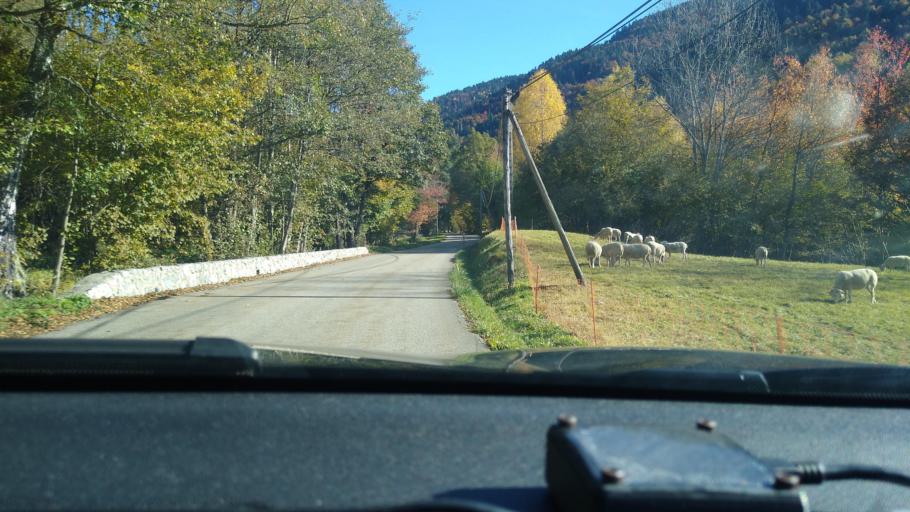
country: FR
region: Midi-Pyrenees
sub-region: Departement de l'Ariege
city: Ax-les-Thermes
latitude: 42.7214
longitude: 1.9039
